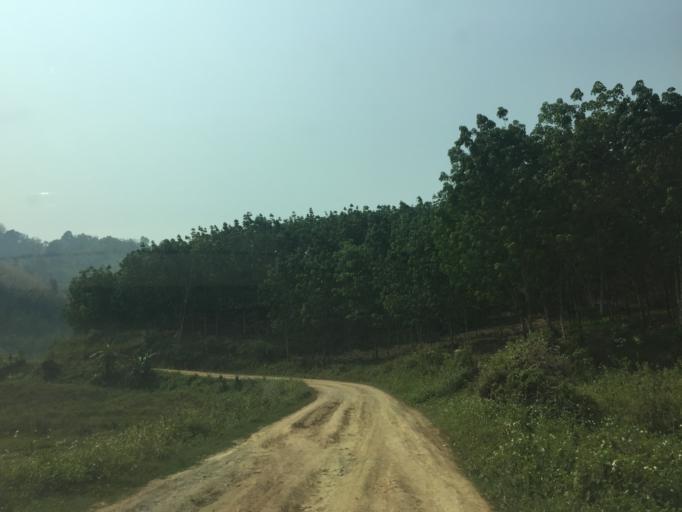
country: TH
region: Phayao
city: Phu Sang
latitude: 19.6014
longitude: 100.5331
